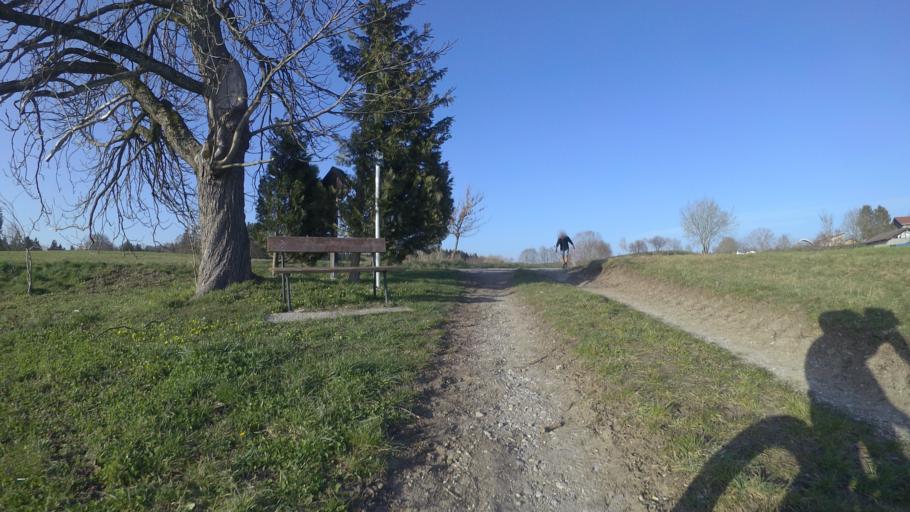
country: DE
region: Bavaria
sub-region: Upper Bavaria
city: Nussdorf
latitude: 47.9203
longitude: 12.5649
